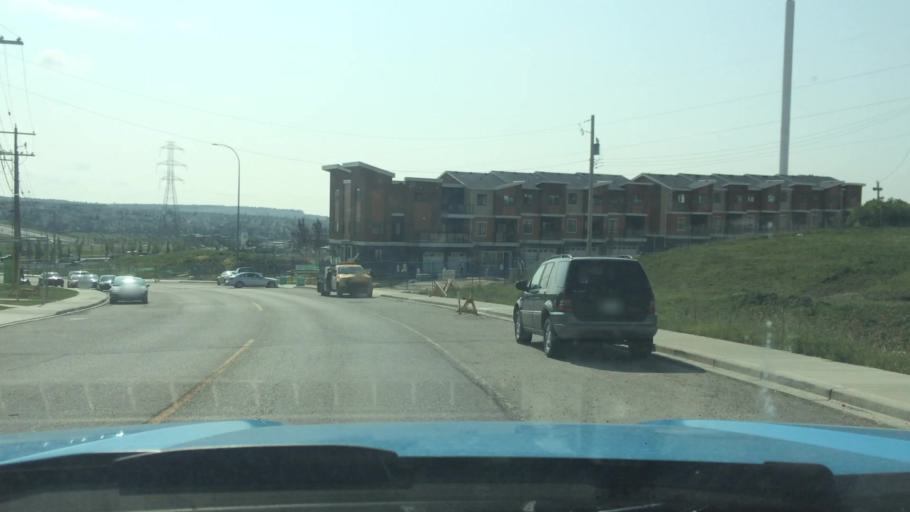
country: CA
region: Alberta
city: Calgary
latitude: 51.1701
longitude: -114.1361
